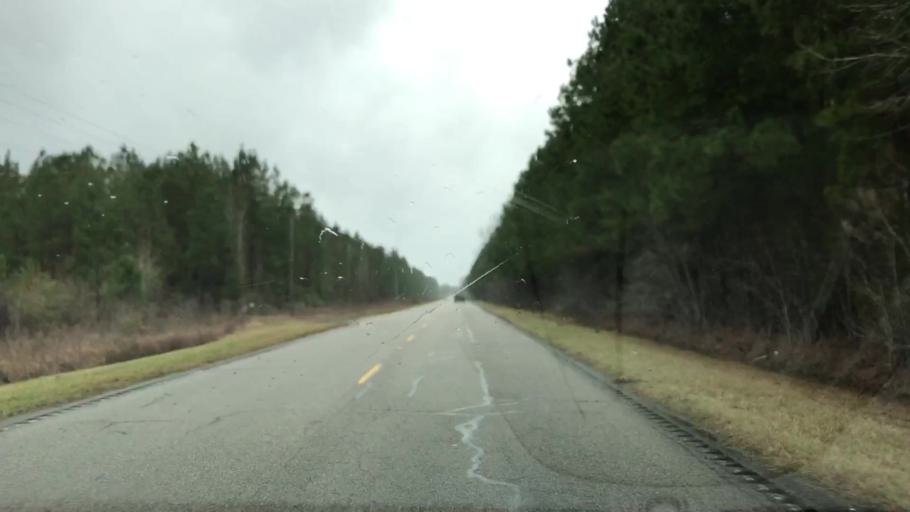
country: US
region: South Carolina
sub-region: Williamsburg County
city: Andrews
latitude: 33.5453
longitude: -79.4729
